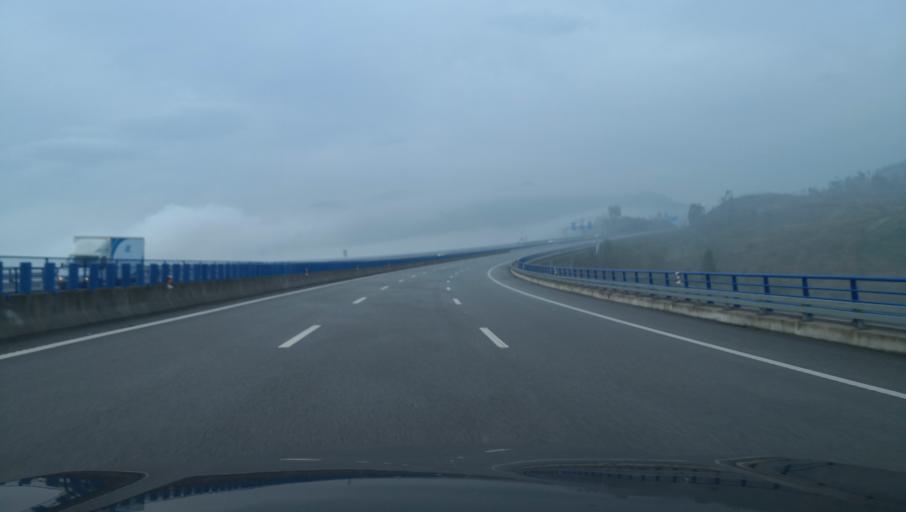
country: PT
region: Porto
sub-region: Paredes
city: Recarei
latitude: 41.1363
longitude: -8.4258
